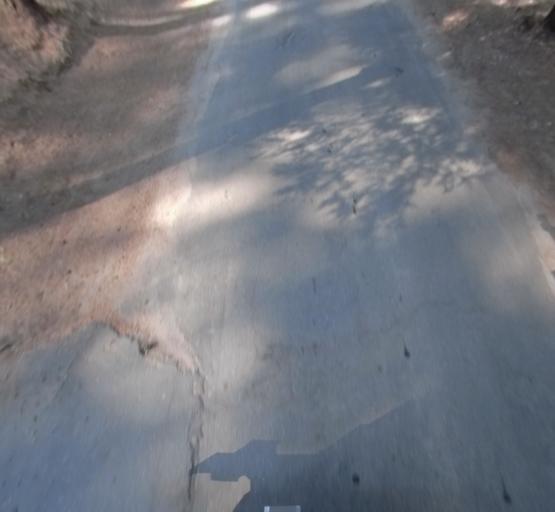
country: US
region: California
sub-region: Madera County
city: Oakhurst
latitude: 37.4023
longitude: -119.6223
